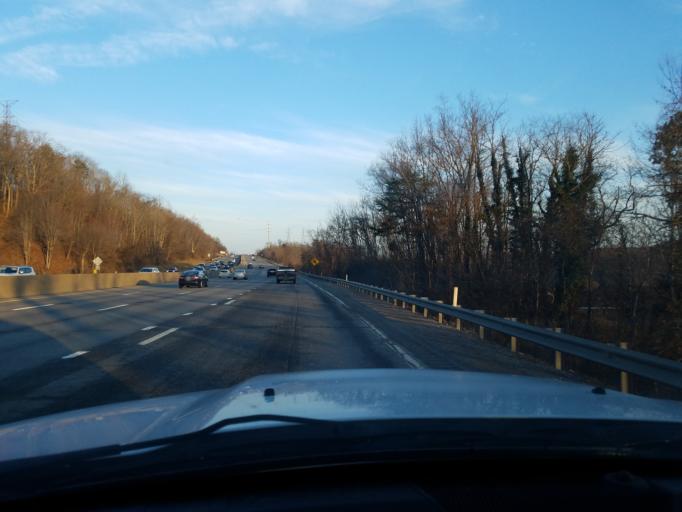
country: US
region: West Virginia
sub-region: Kanawha County
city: Cross Lanes
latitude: 38.4197
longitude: -81.8019
